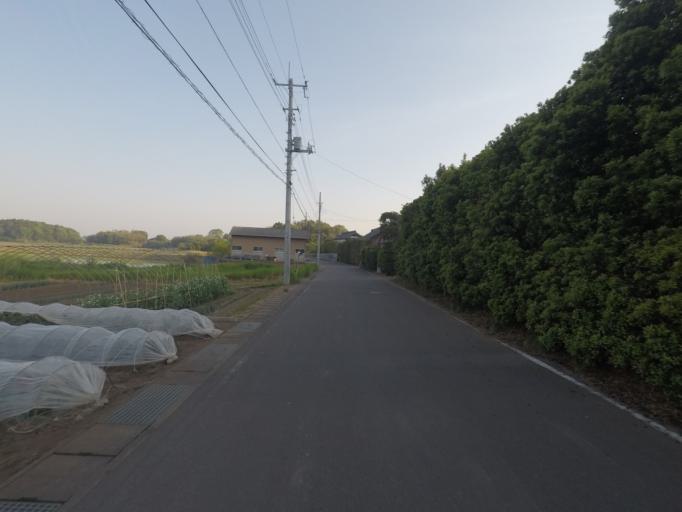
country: JP
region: Ibaraki
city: Naka
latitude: 36.0966
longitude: 140.1318
